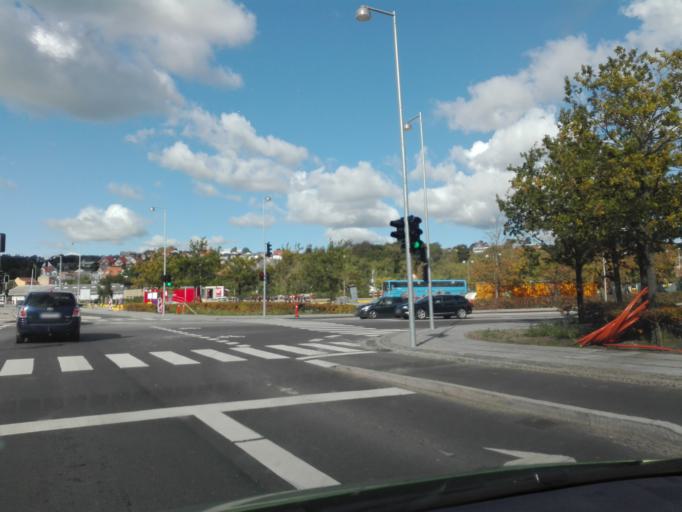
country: DK
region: North Denmark
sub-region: Mariagerfjord Kommune
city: Hobro
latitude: 56.6390
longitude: 9.7977
